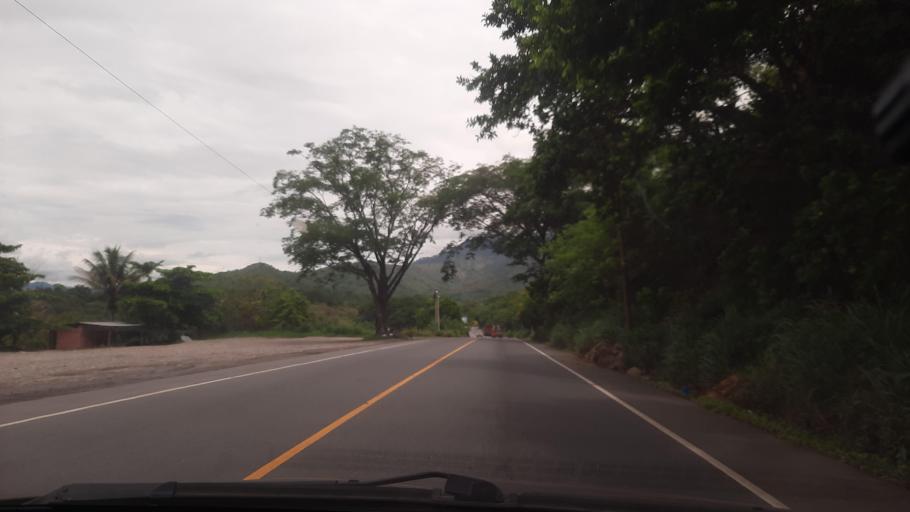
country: GT
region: Zacapa
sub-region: Municipio de Zacapa
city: Gualan
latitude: 15.1832
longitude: -89.2940
